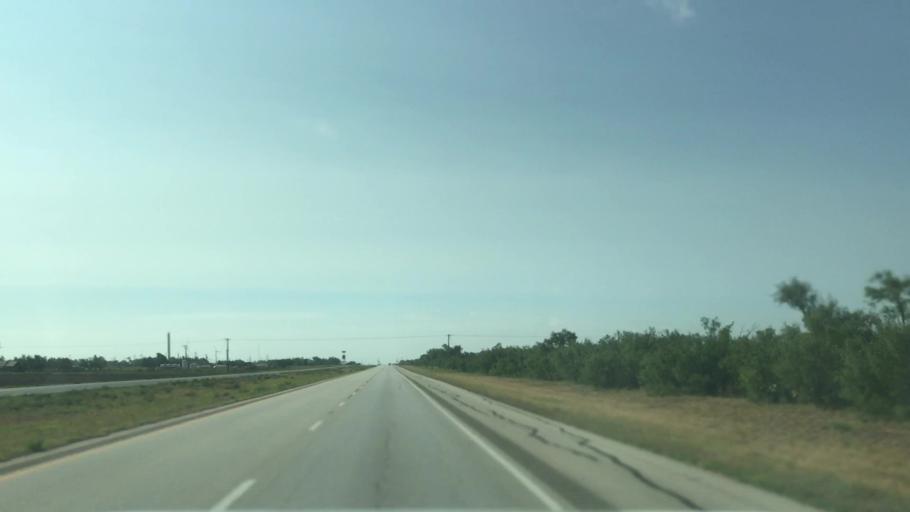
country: US
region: Texas
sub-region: Scurry County
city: Snyder
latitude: 32.6429
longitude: -100.7705
